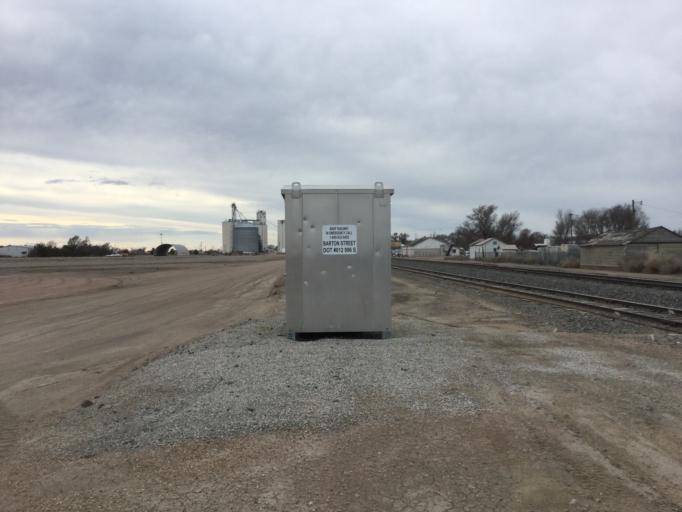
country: US
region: Kansas
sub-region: Hamilton County
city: Syracuse
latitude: 37.9766
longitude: -101.7429
